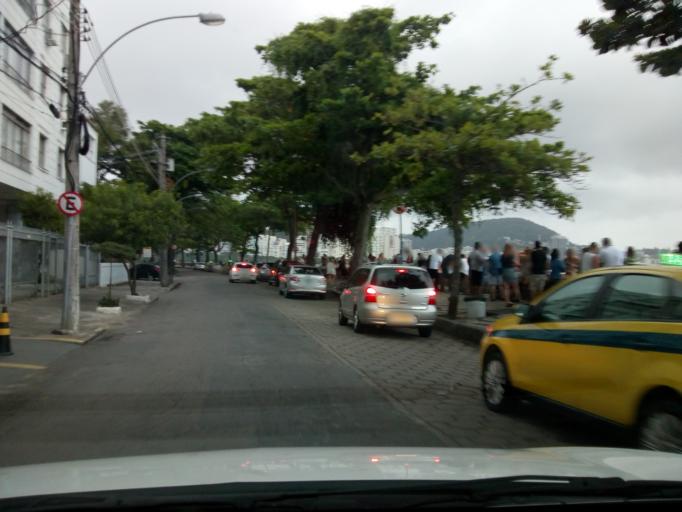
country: BR
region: Rio de Janeiro
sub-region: Rio De Janeiro
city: Rio de Janeiro
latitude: -22.9435
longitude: -43.1601
